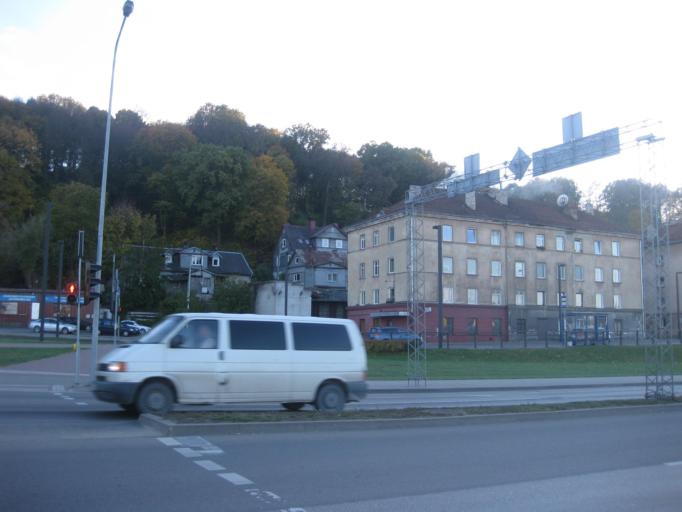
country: LT
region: Kauno apskritis
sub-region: Kaunas
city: Kaunas
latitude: 54.8928
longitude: 23.8900
